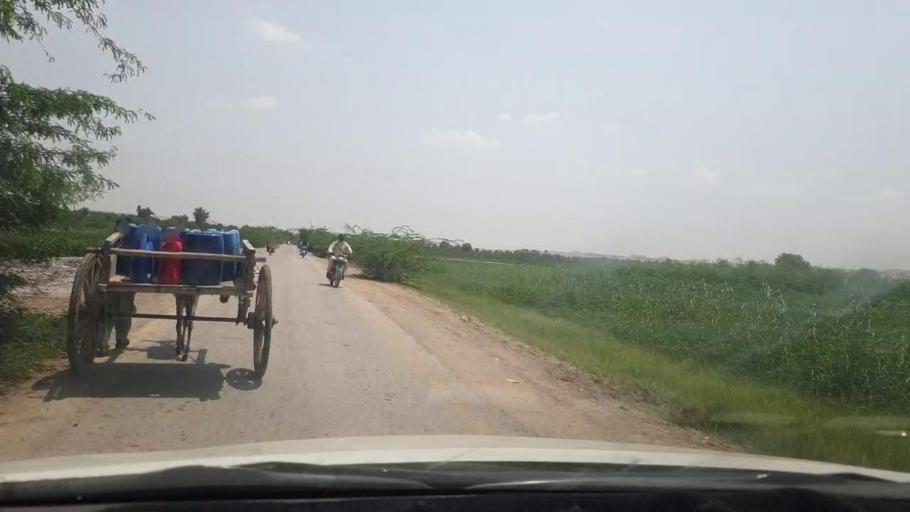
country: PK
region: Sindh
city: Khairpur
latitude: 27.5350
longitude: 68.8878
